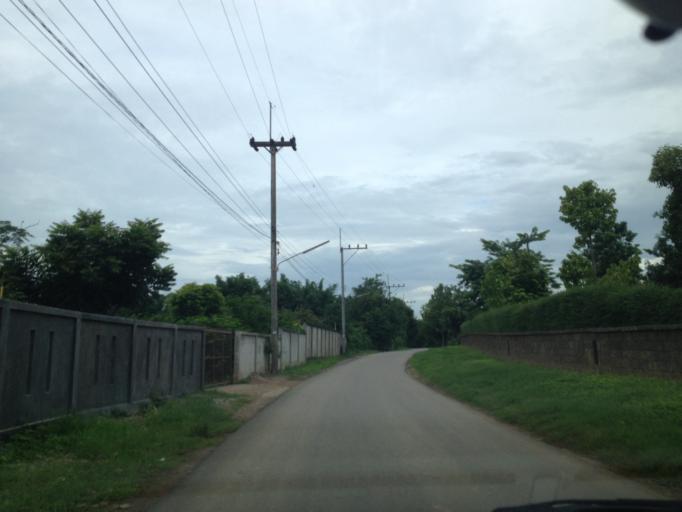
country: TH
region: Chiang Mai
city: Hang Dong
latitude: 18.7256
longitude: 98.9050
